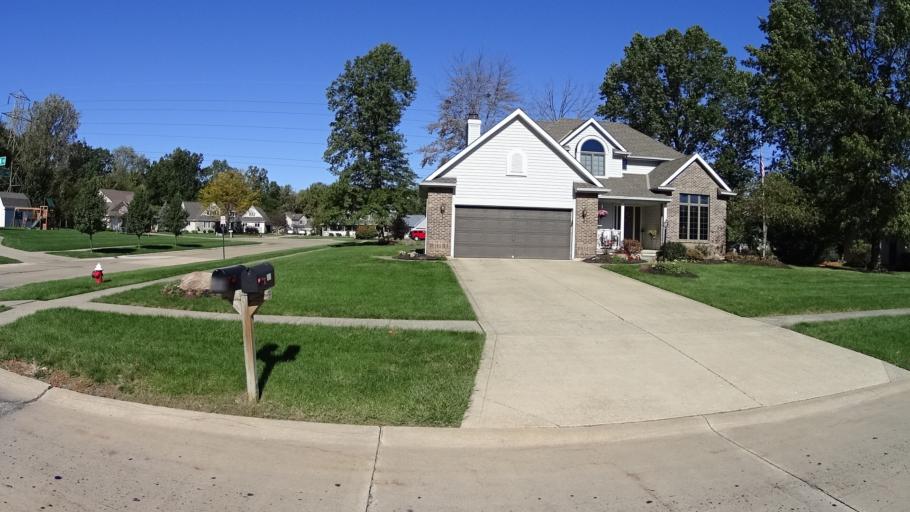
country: US
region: Ohio
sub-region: Lorain County
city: Amherst
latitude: 41.4036
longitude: -82.2490
